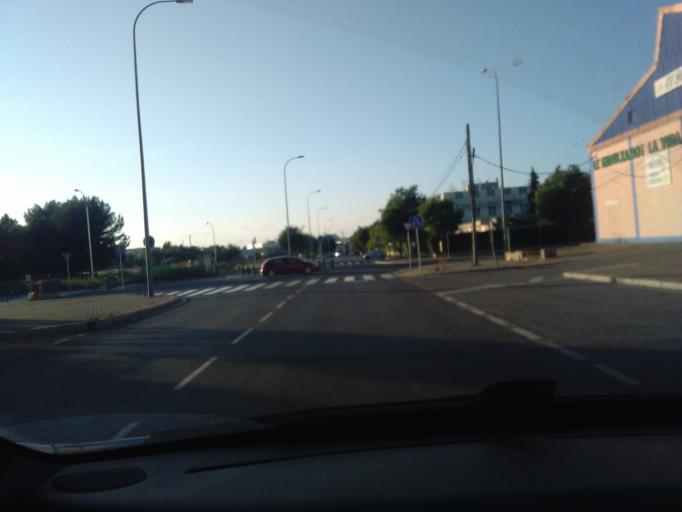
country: ES
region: Andalusia
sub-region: Provincia de Sevilla
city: Sevilla
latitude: 37.3921
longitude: -5.9458
